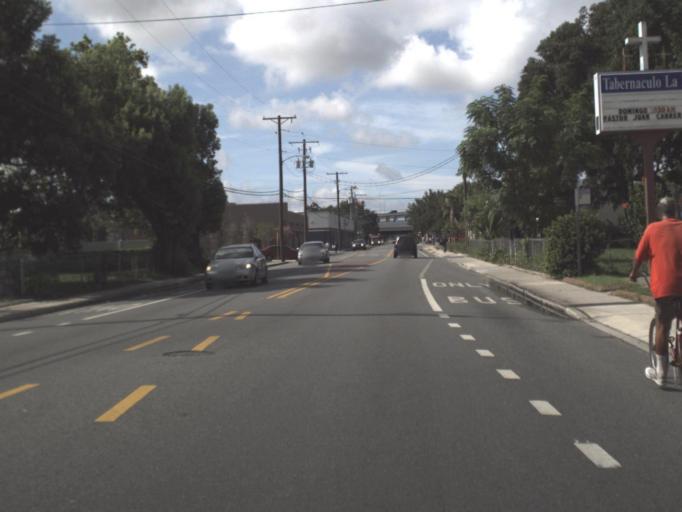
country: US
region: Florida
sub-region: Hillsborough County
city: Tampa
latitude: 27.9689
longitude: -82.4512
